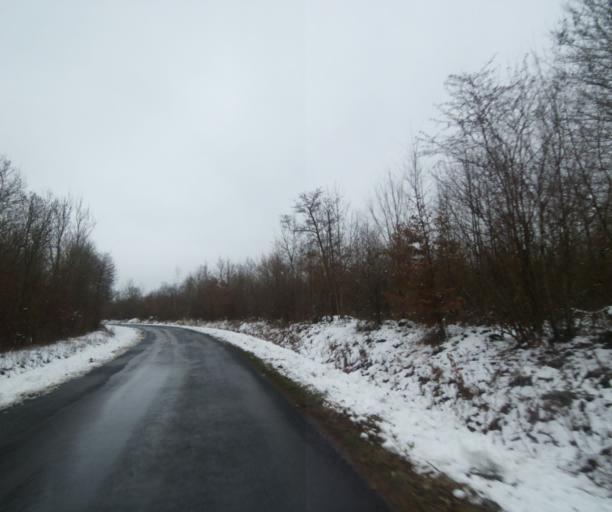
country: FR
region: Champagne-Ardenne
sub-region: Departement de la Haute-Marne
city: Laneuville-a-Remy
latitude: 48.4867
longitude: 4.8659
